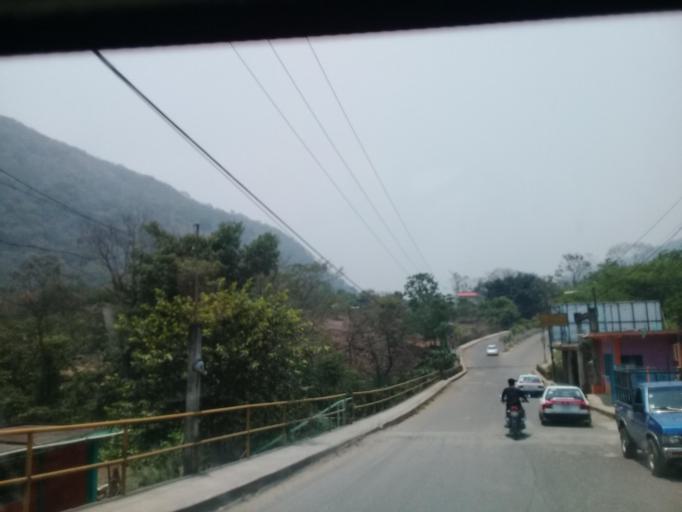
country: MX
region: Veracruz
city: Tezonapa
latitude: 18.6065
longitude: -96.6886
